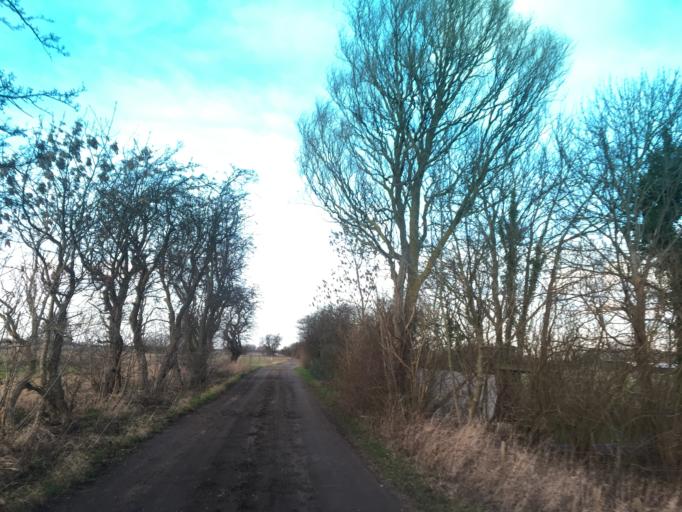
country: DK
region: Capital Region
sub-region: Tarnby Kommune
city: Tarnby
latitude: 55.5942
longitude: 12.6212
